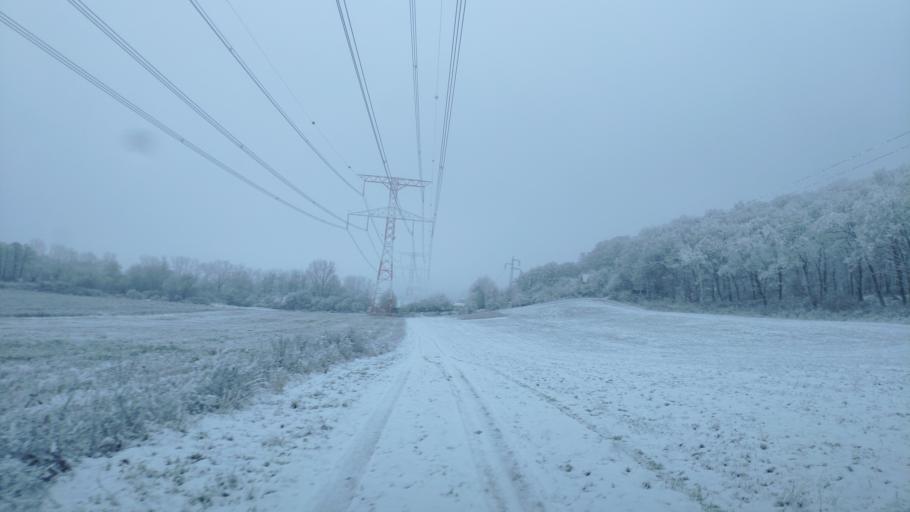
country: SK
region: Kosicky
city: Kosice
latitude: 48.6470
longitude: 21.1713
